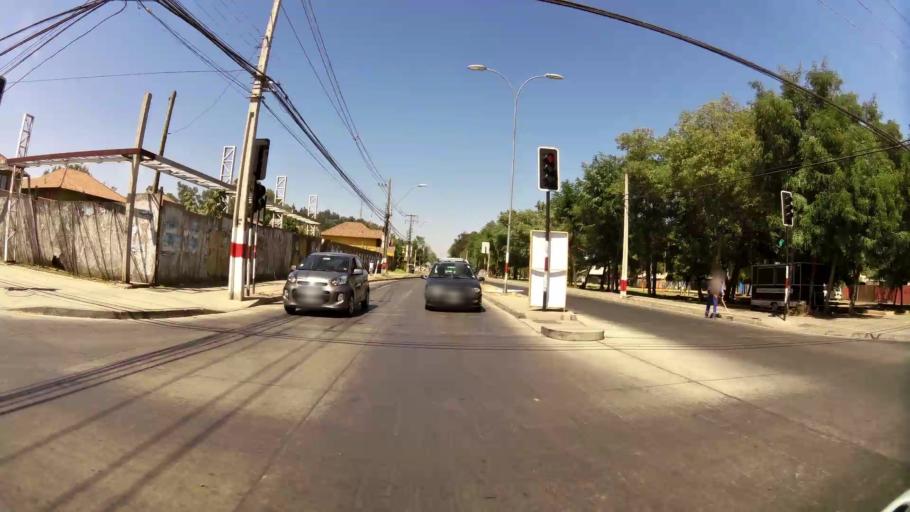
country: CL
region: Maule
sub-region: Provincia de Curico
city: Curico
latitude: -34.9705
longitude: -71.2307
